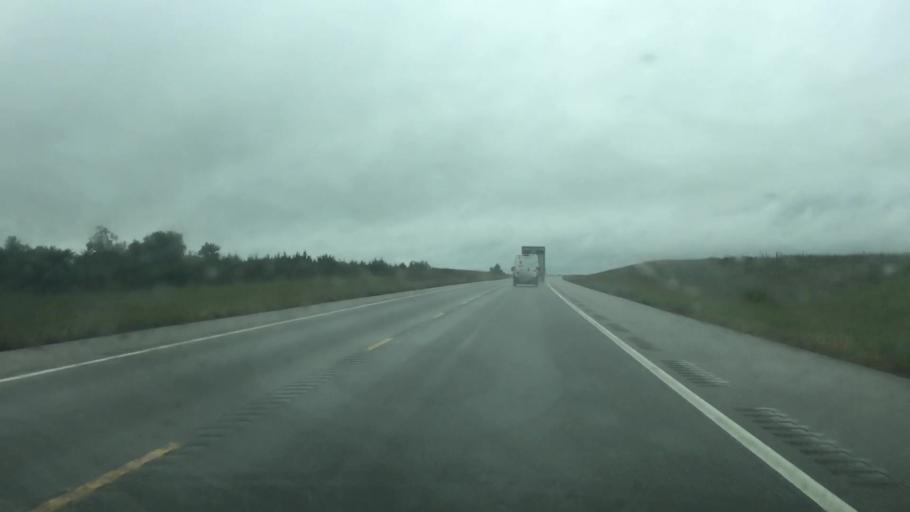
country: US
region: Kansas
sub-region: Allen County
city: Iola
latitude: 38.0917
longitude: -95.3624
